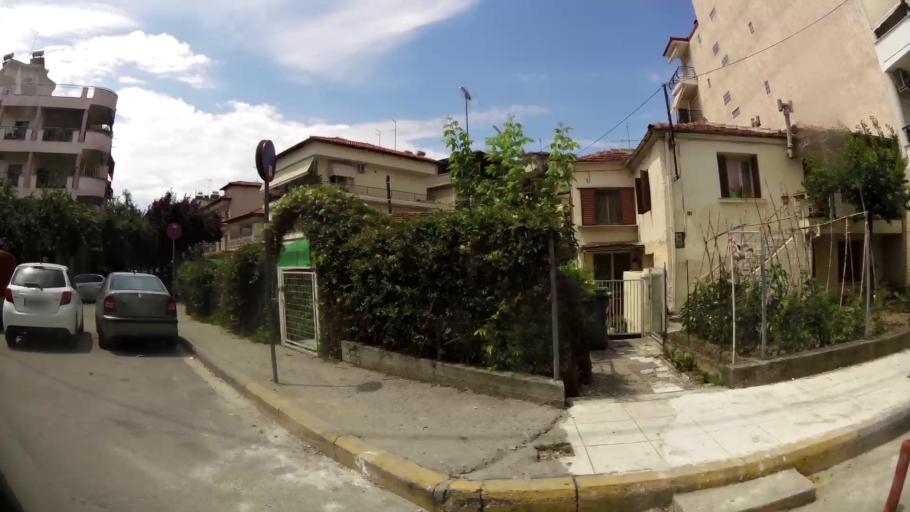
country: GR
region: Central Macedonia
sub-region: Nomos Pierias
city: Katerini
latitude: 40.2679
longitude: 22.5100
